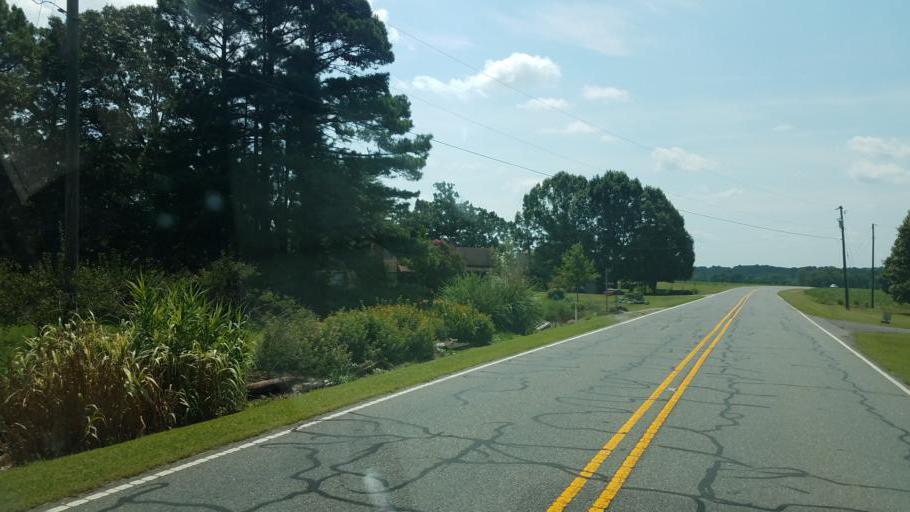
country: US
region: North Carolina
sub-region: Gaston County
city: Cherryville
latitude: 35.4286
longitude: -81.4134
